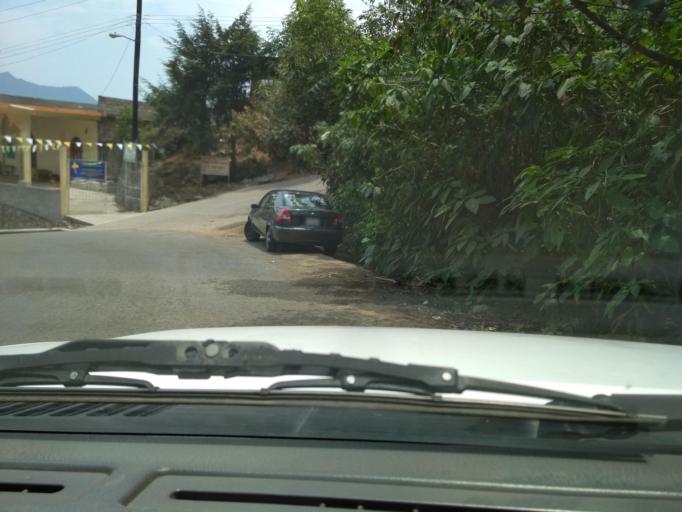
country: MX
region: Veracruz
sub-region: Camerino Z. Mendoza
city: La Cuesta
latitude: 18.7920
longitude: -97.1716
